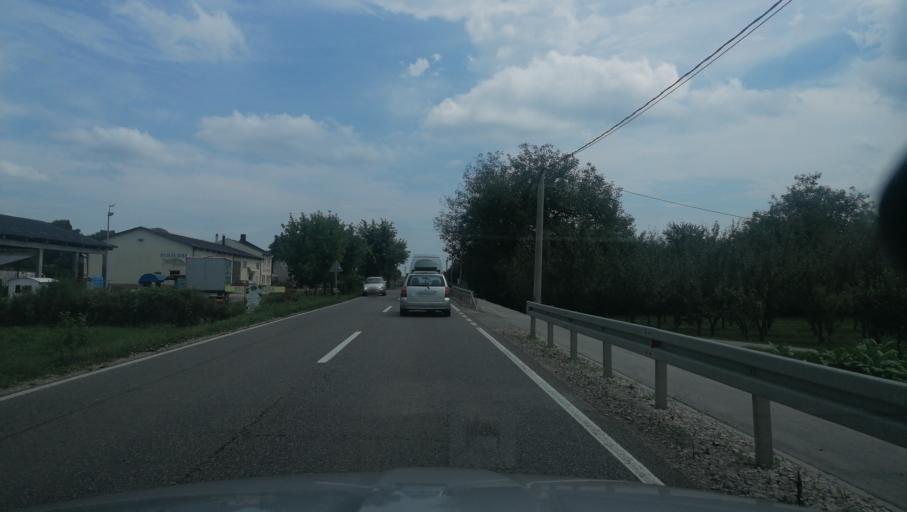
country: BA
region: Republika Srpska
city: Obudovac
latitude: 44.9591
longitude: 18.6273
